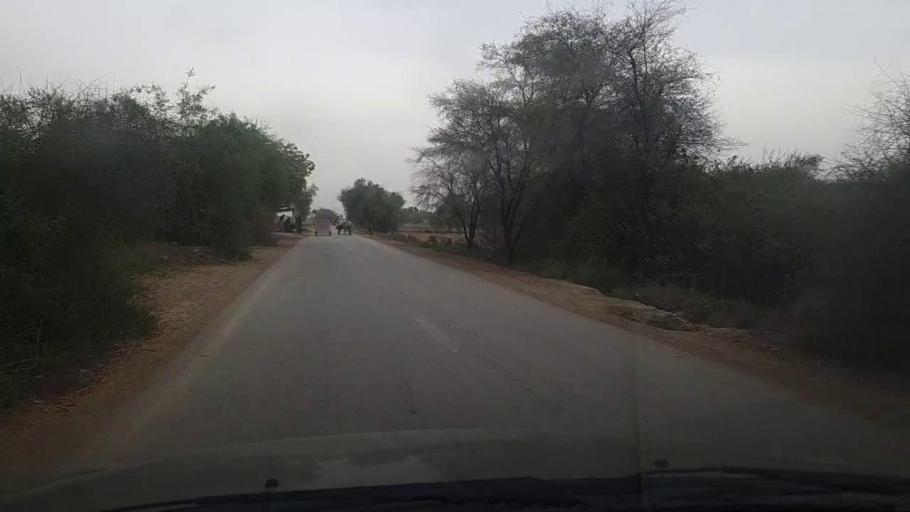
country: PK
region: Sindh
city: Daulatpur
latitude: 26.3292
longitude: 68.1123
